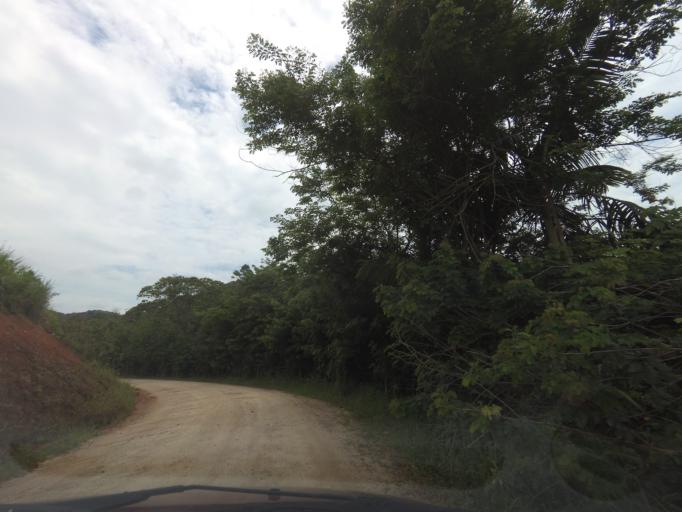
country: BR
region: Santa Catarina
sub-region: Blumenau
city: Blumenau
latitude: -26.9718
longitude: -49.0247
